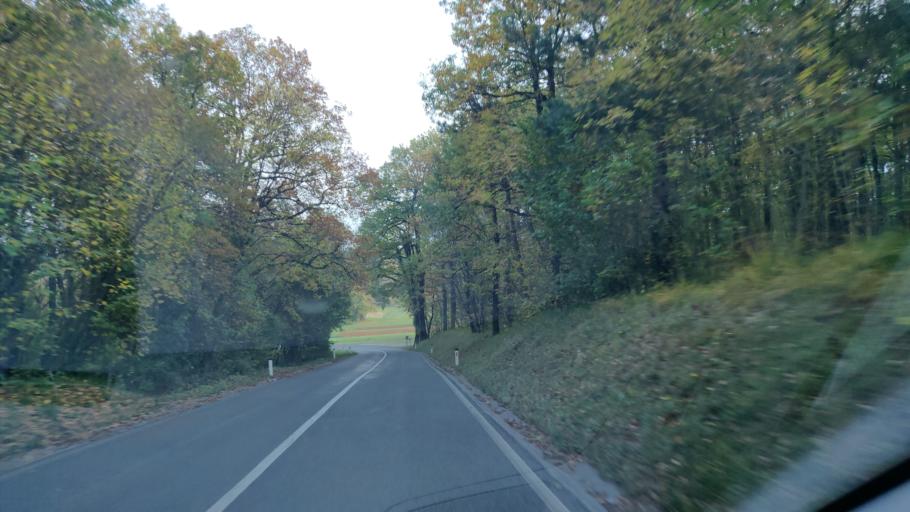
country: SI
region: Komen
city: Komen
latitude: 45.8175
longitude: 13.7642
